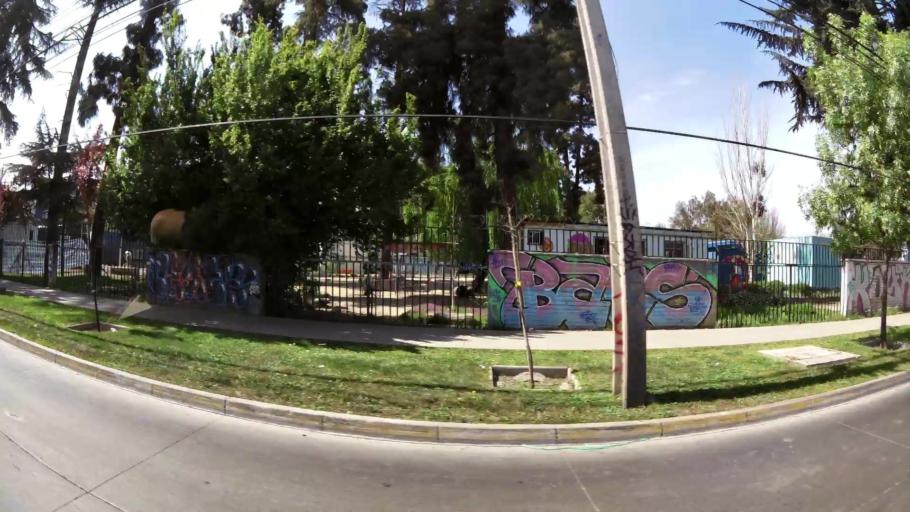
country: CL
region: Santiago Metropolitan
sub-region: Provincia de Cordillera
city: Puente Alto
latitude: -33.5753
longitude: -70.5823
